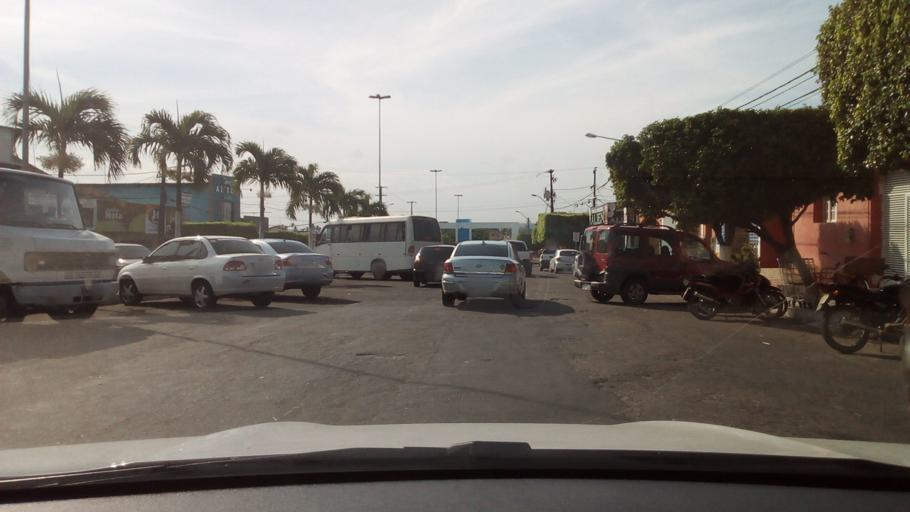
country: BR
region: Rio Grande do Norte
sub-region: Goianinha
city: Goianinha
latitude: -6.2666
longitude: -35.2086
